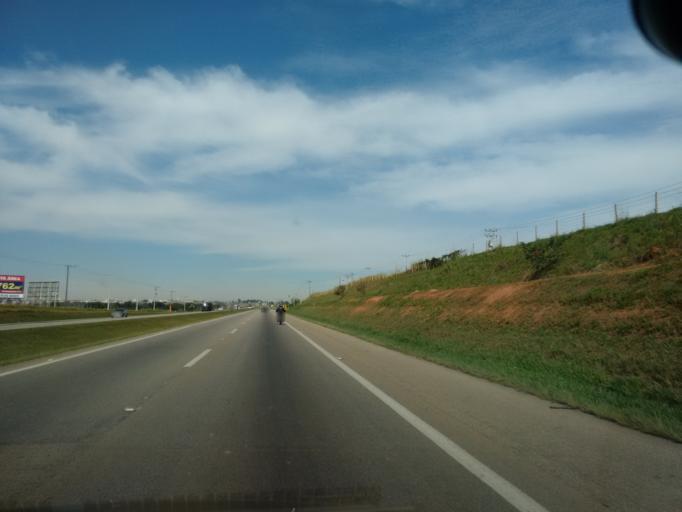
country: BR
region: Sao Paulo
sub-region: Itu
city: Itu
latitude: -23.2864
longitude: -47.3293
